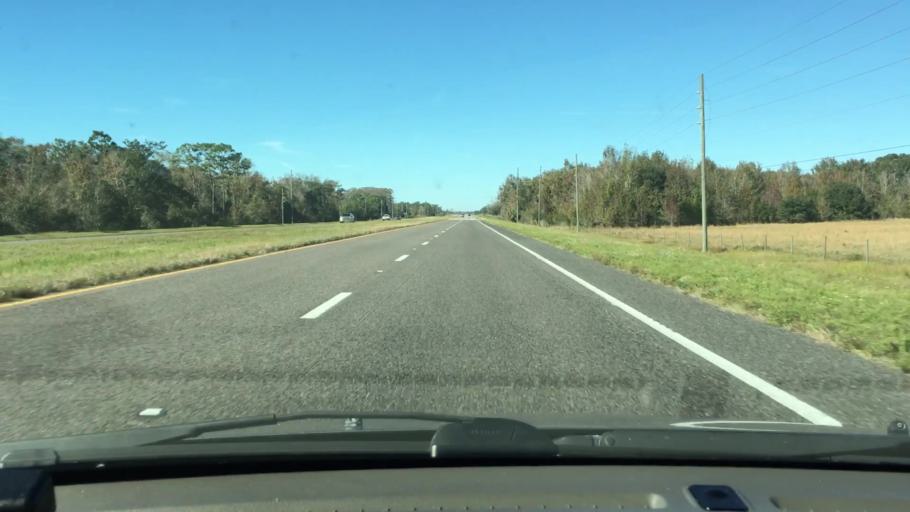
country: US
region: Florida
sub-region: Brevard County
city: June Park
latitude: 28.1230
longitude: -80.9593
